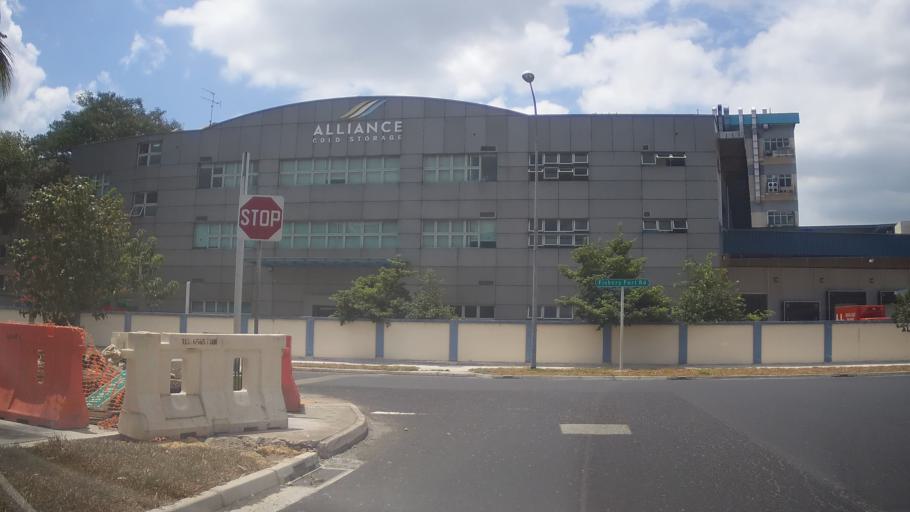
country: SG
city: Singapore
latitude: 1.3105
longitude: 103.7227
